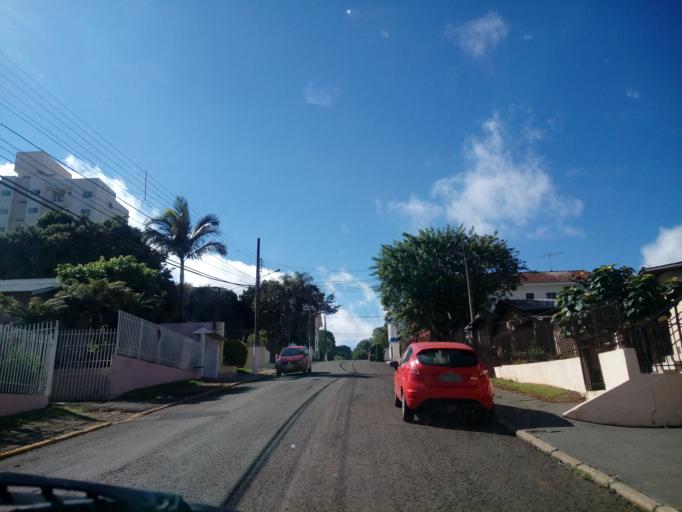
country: BR
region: Santa Catarina
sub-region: Chapeco
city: Chapeco
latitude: -27.1154
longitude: -52.6177
